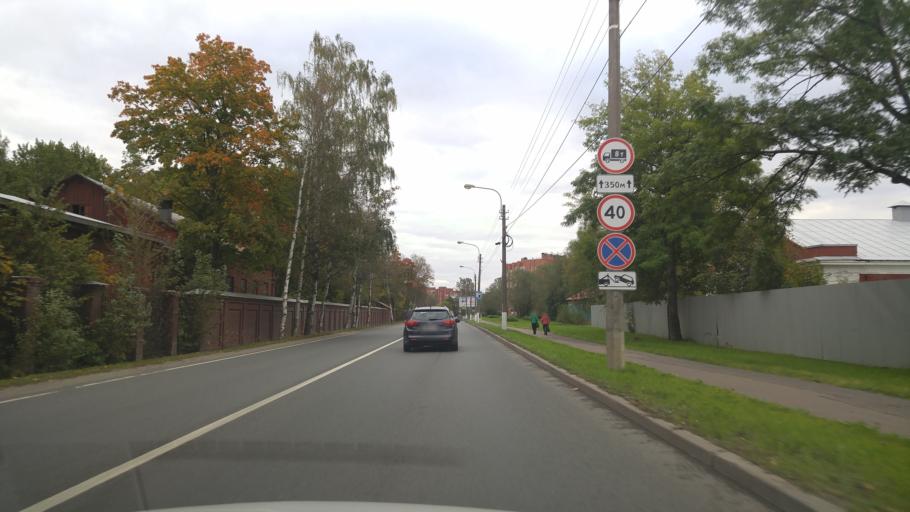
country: RU
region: St.-Petersburg
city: Kronshtadt
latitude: 60.0040
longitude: 29.7529
